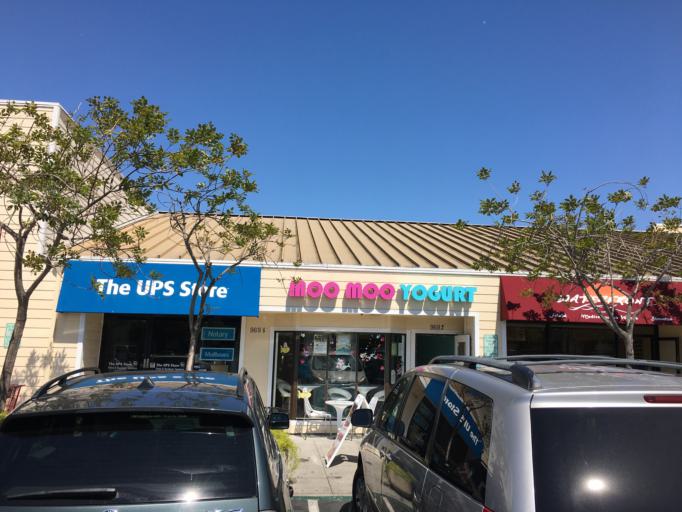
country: US
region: California
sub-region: San Mateo County
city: Foster City
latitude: 37.5442
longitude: -122.2708
